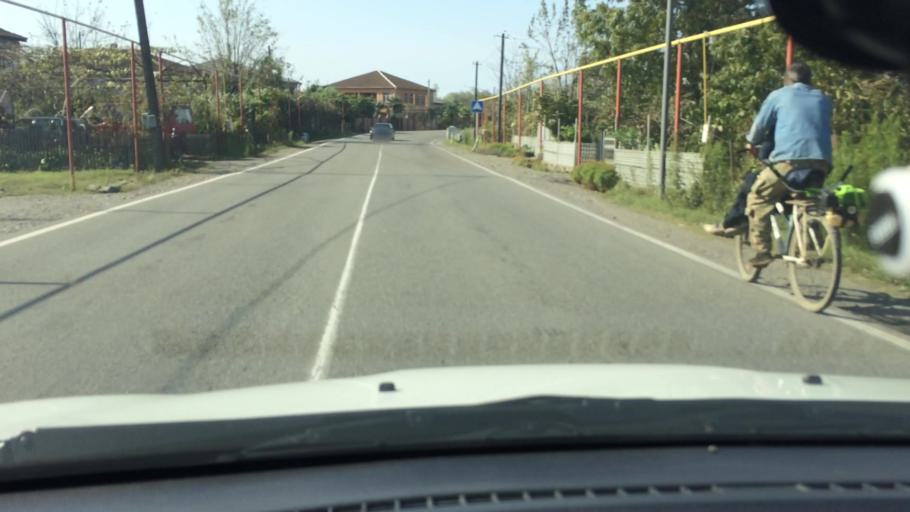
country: GE
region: Guria
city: Urek'i
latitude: 42.0399
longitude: 41.8063
